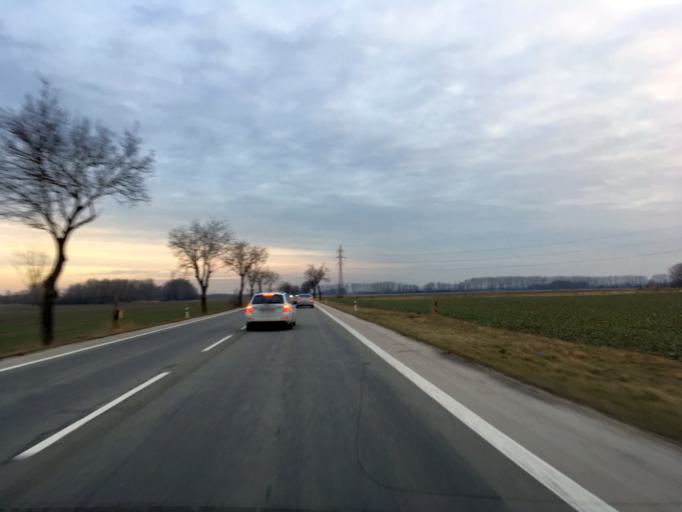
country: SK
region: Trnavsky
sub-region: Okres Dunajska Streda
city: Velky Meder
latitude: 47.8990
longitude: 17.7415
